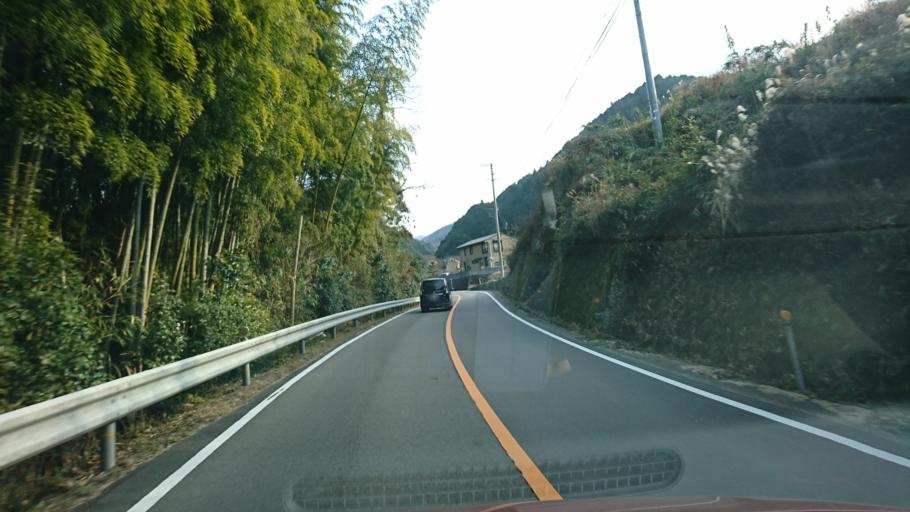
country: JP
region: Ehime
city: Hojo
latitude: 33.9700
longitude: 132.9027
